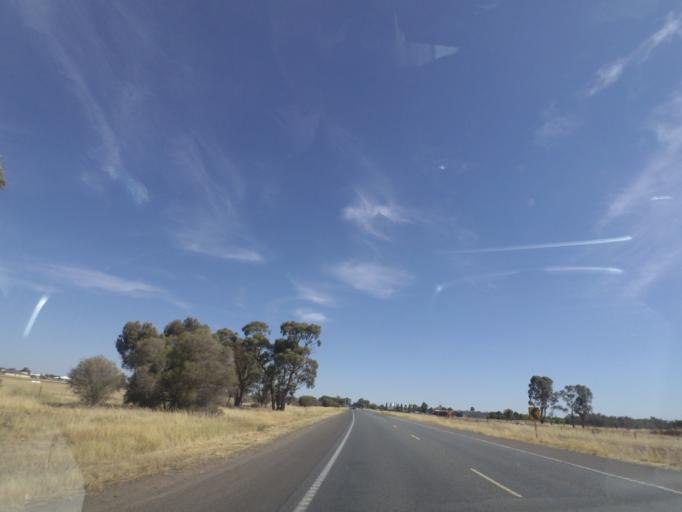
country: AU
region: Victoria
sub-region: Greater Shepparton
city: Shepparton
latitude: -36.4315
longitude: 145.3888
